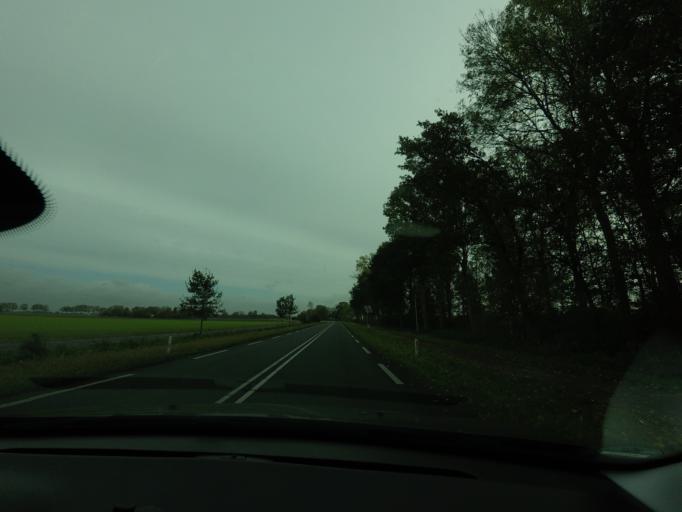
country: NL
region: Flevoland
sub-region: Gemeente Noordoostpolder
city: Ens
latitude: 52.7089
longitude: 5.8248
